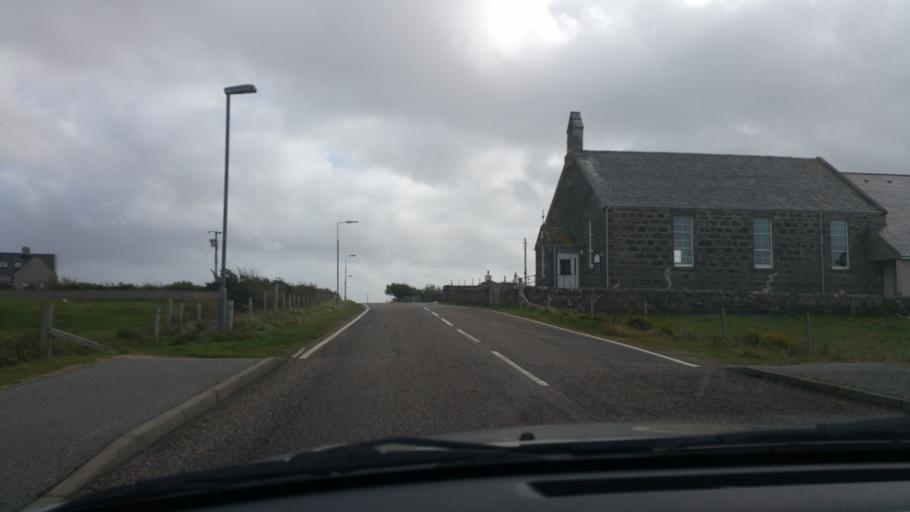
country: GB
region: Scotland
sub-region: Eilean Siar
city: Isle of North Uist
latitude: 57.5519
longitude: -7.3331
